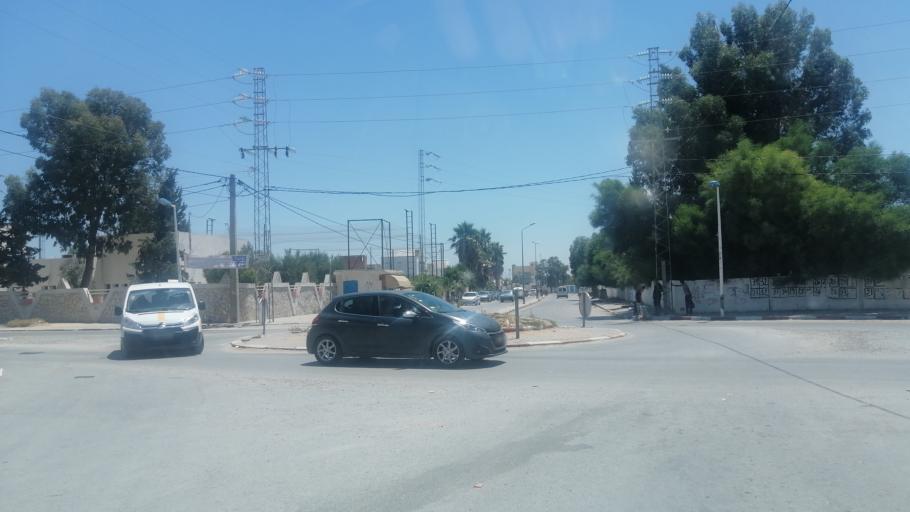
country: TN
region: Al Qayrawan
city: Sbikha
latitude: 36.1218
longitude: 10.0888
